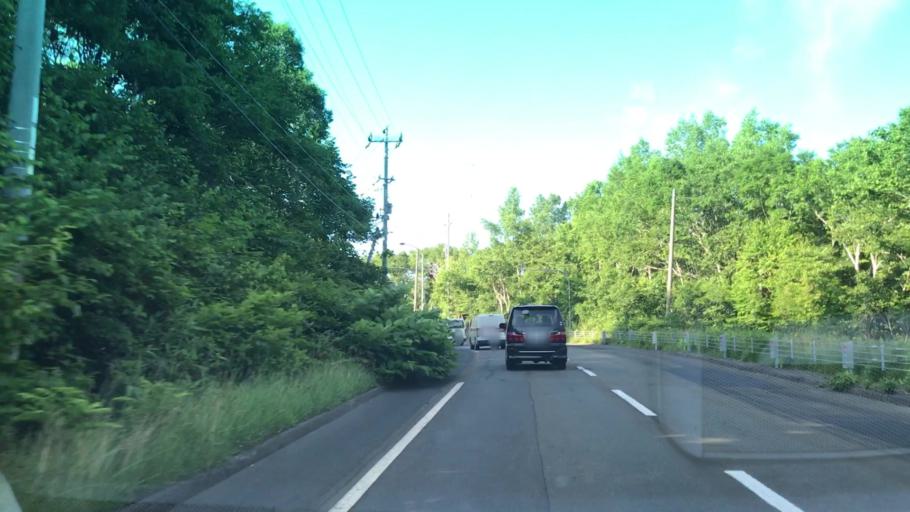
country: JP
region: Hokkaido
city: Otaru
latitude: 43.1281
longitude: 141.0129
